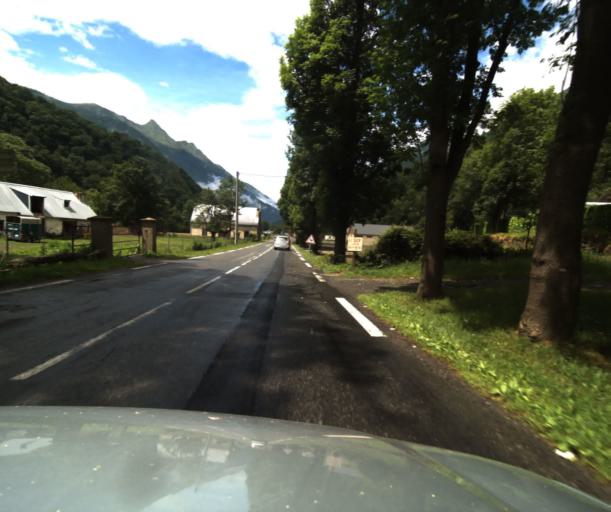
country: FR
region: Midi-Pyrenees
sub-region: Departement des Hautes-Pyrenees
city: Luz-Saint-Sauveur
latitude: 42.8836
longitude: -0.0142
